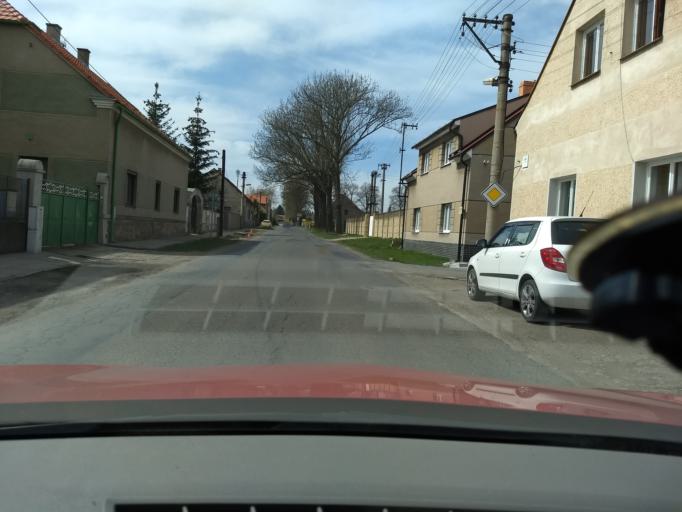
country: CZ
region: Central Bohemia
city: Rudna
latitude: 50.0459
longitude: 14.1848
